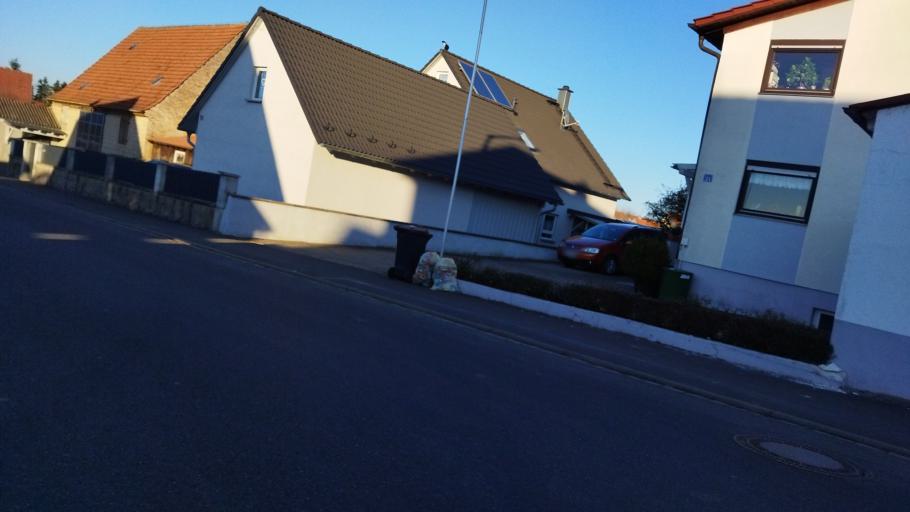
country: DE
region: Bavaria
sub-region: Regierungsbezirk Unterfranken
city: Dettelbach
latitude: 49.7929
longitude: 10.1693
